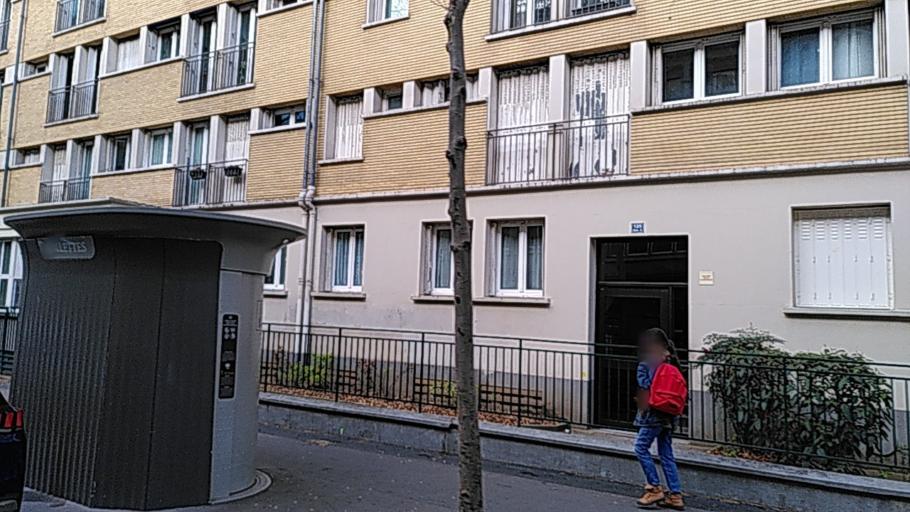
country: FR
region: Ile-de-France
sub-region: Paris
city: Paris
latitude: 48.8542
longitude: 2.3782
